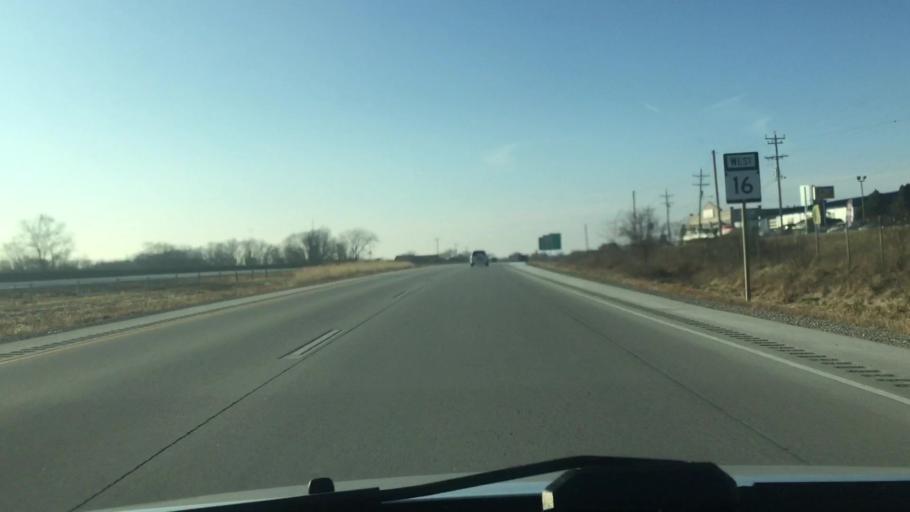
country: US
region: Wisconsin
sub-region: Waukesha County
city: Nashotah
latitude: 43.1020
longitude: -88.4131
